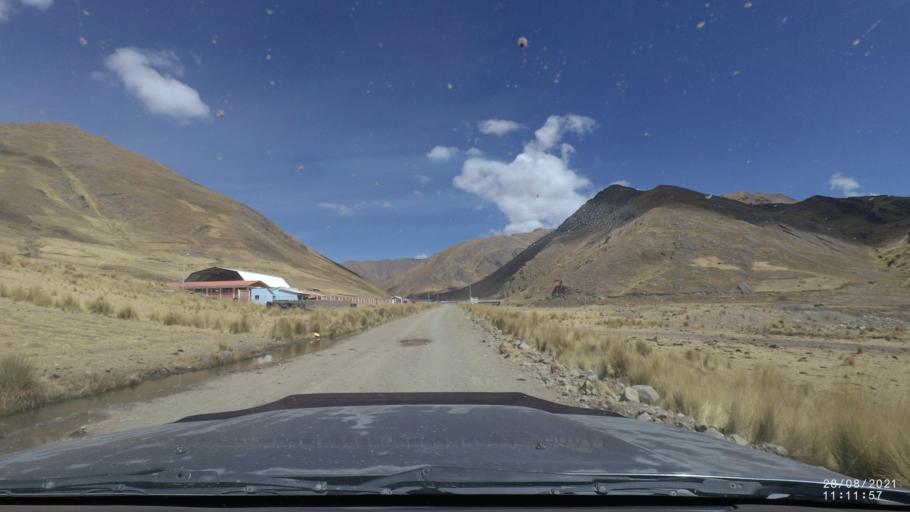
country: BO
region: Cochabamba
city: Cochabamba
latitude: -17.1489
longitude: -66.3158
